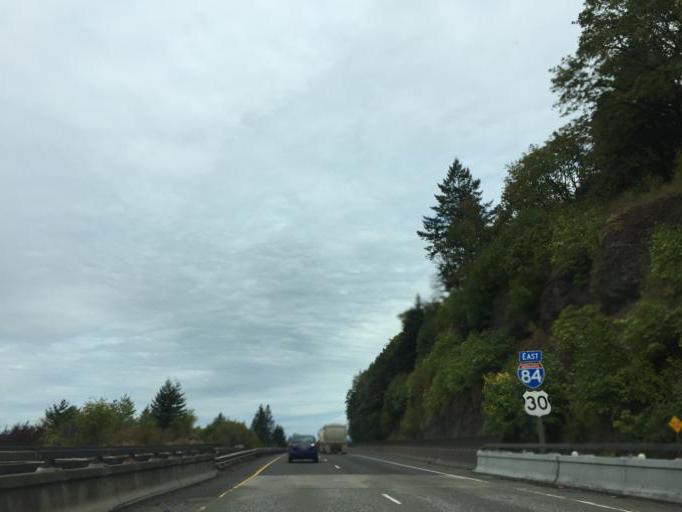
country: US
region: Oregon
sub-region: Hood River County
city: Cascade Locks
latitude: 45.6146
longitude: -121.9972
